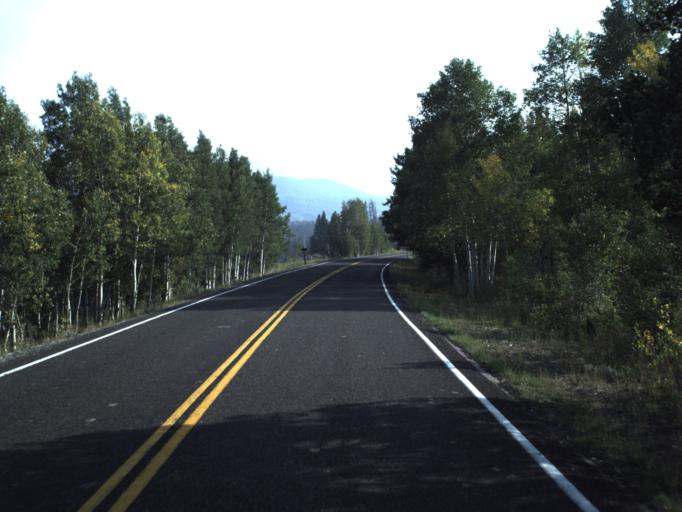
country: US
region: Wyoming
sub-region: Uinta County
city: Evanston
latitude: 40.8407
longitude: -110.8476
